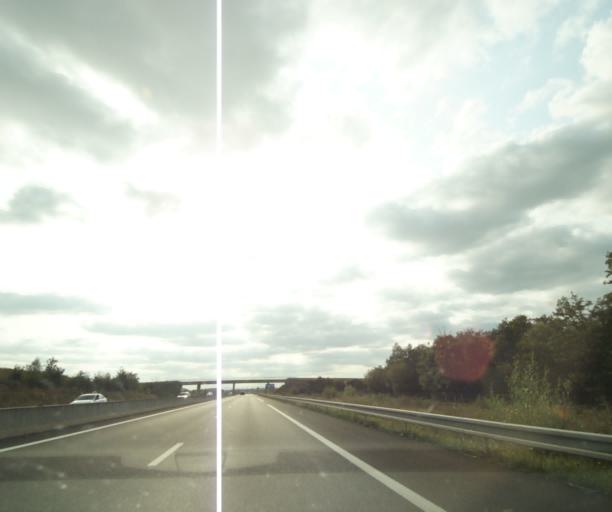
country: FR
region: Centre
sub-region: Departement d'Indre-et-Loire
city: Veigne
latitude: 47.3138
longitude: 0.7426
